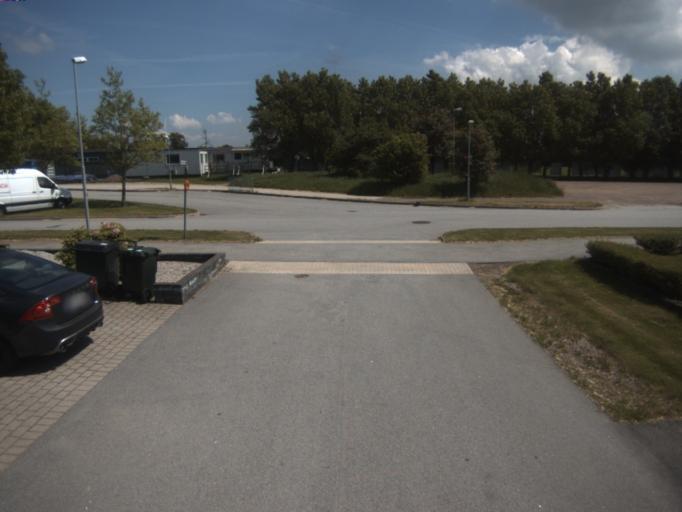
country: SE
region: Skane
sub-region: Helsingborg
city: Barslov
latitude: 56.0295
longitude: 12.8071
